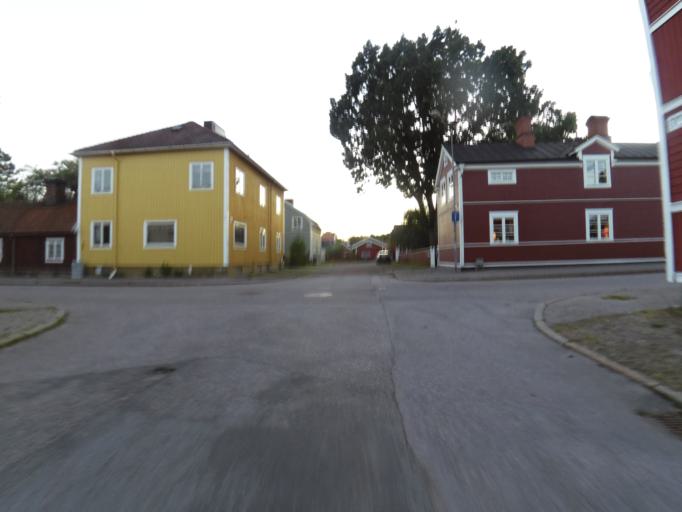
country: SE
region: Gaevleborg
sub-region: Gavle Kommun
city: Gavle
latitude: 60.7018
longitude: 17.1628
